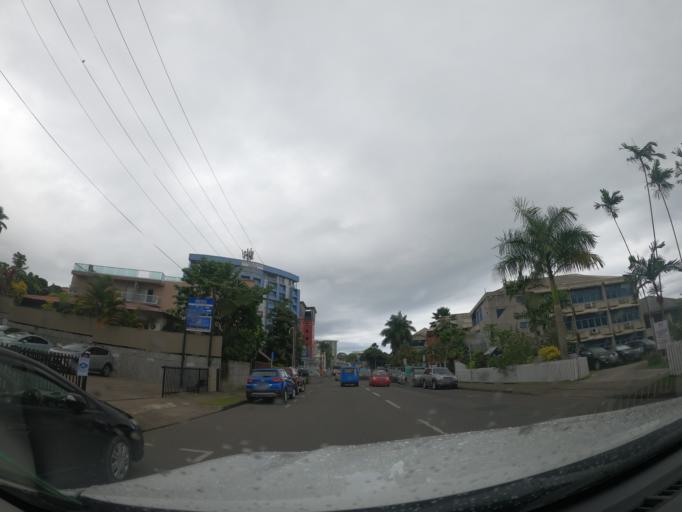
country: FJ
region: Central
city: Suva
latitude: -18.1432
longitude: 178.4257
